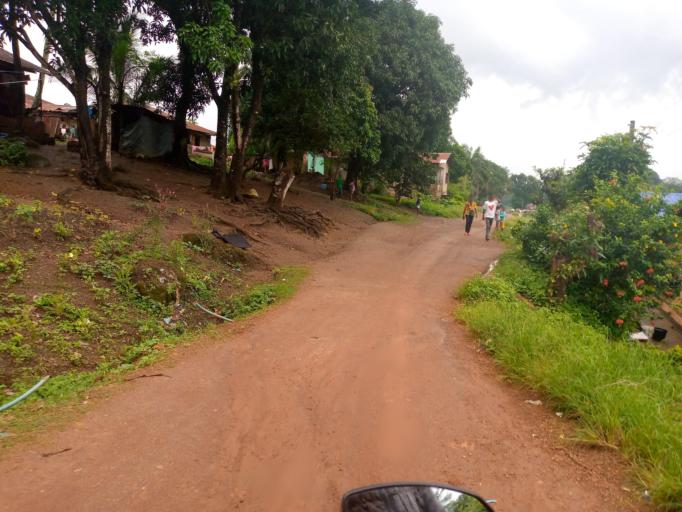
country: SL
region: Eastern Province
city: Kenema
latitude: 7.8804
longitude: -11.1814
